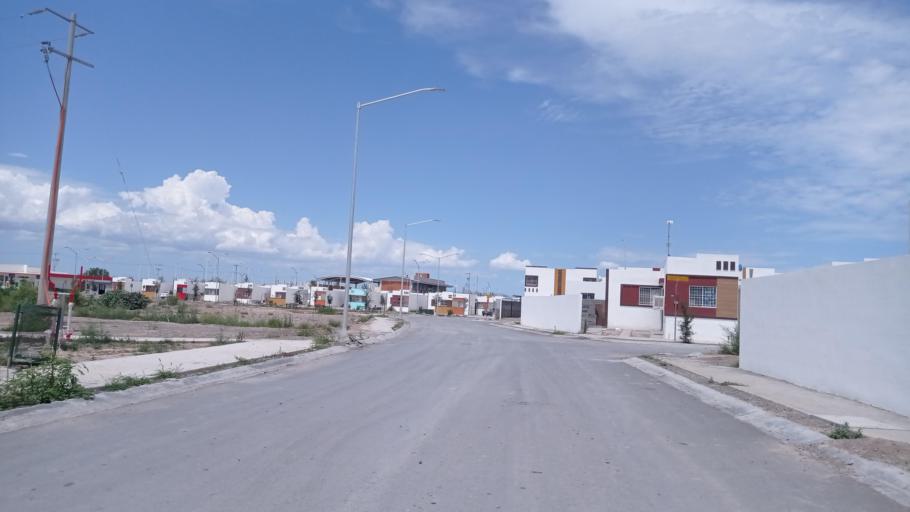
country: MX
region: Nuevo Leon
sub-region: Salinas Victoria
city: Simeprodeso (Colectivo Nuevo)
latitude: 25.8749
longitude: -100.3206
